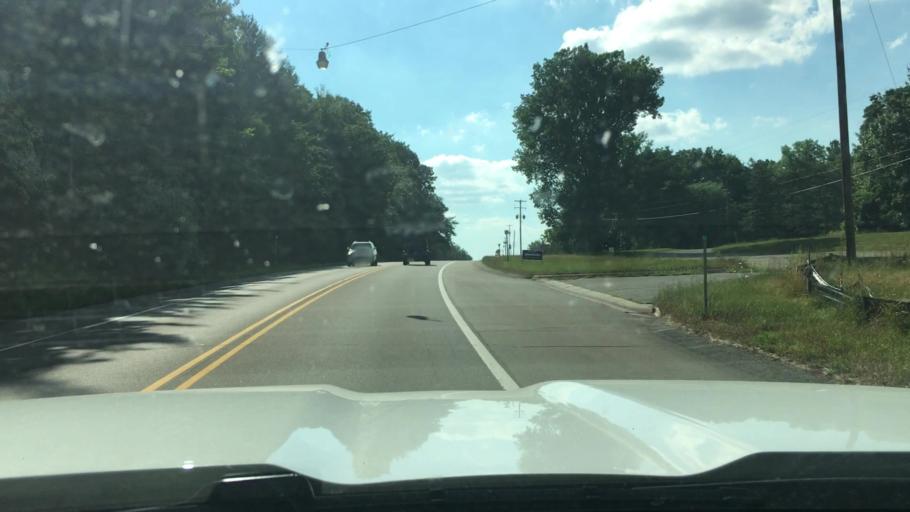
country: US
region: Michigan
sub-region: Kent County
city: Rockford
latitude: 43.0843
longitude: -85.4590
